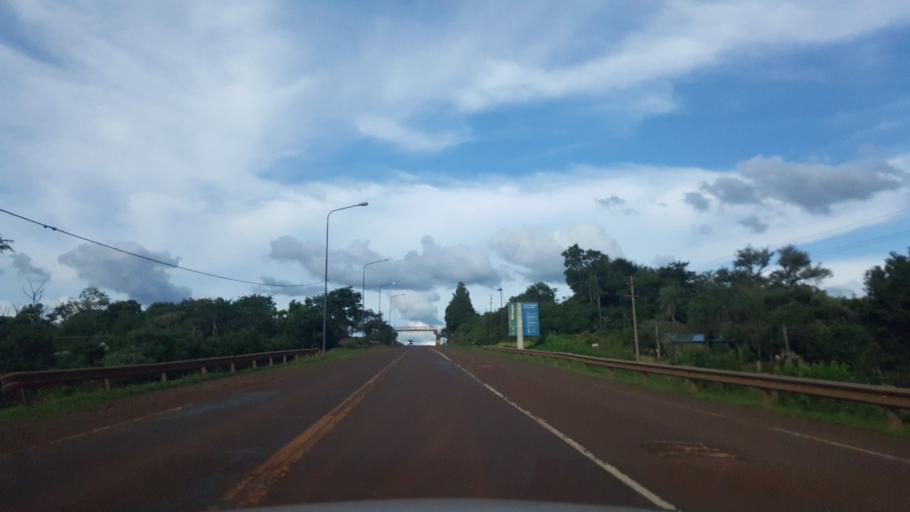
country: AR
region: Misiones
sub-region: Departamento de San Ignacio
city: San Ignacio
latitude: -27.2636
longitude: -55.5346
